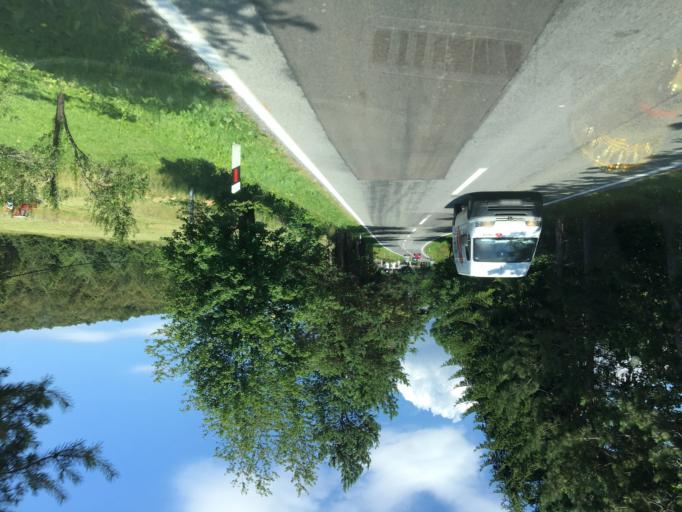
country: HR
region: Licko-Senjska
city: Jezerce
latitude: 44.8651
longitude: 15.6402
